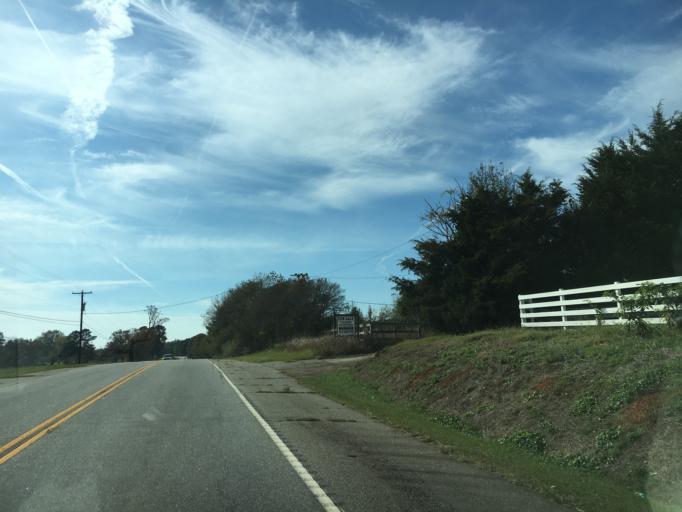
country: US
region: South Carolina
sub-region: Anderson County
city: Belton
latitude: 34.5526
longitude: -82.5627
